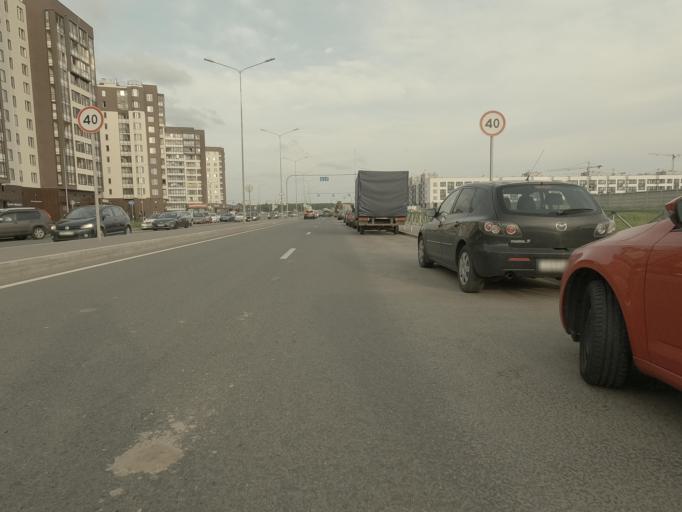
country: RU
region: St.-Petersburg
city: Sosnovaya Polyana
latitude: 59.8365
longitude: 30.1093
